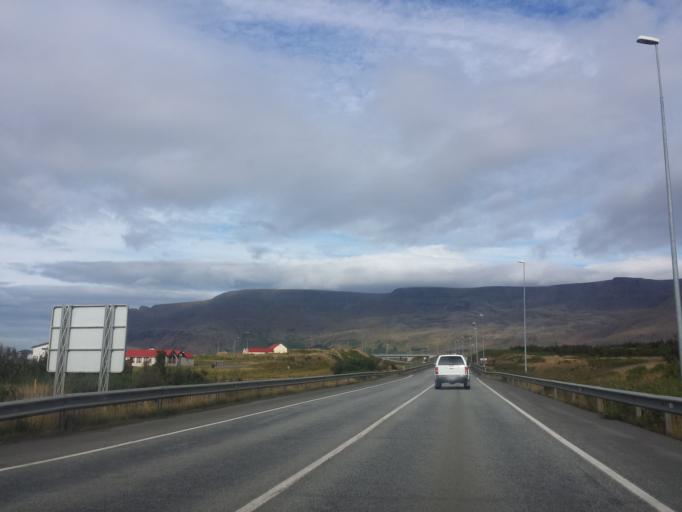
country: IS
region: Capital Region
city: Mosfellsbaer
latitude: 64.1793
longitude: -21.6781
